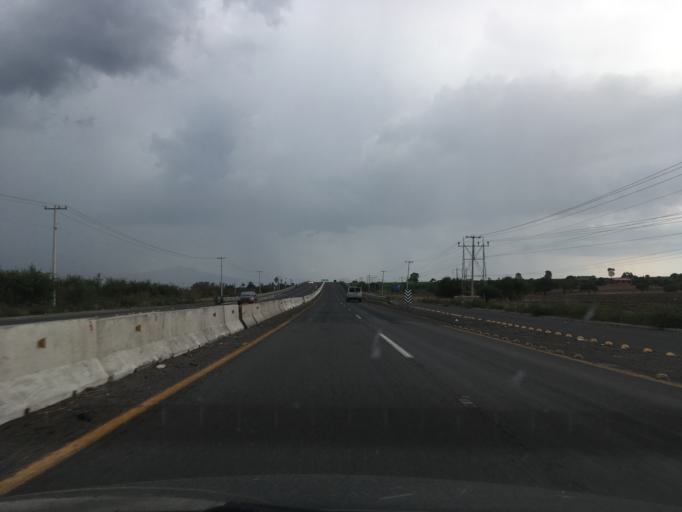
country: MX
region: Guanajuato
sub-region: Tarimoro
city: San Juan Bautista Cacalote
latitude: 20.3495
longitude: -100.8040
